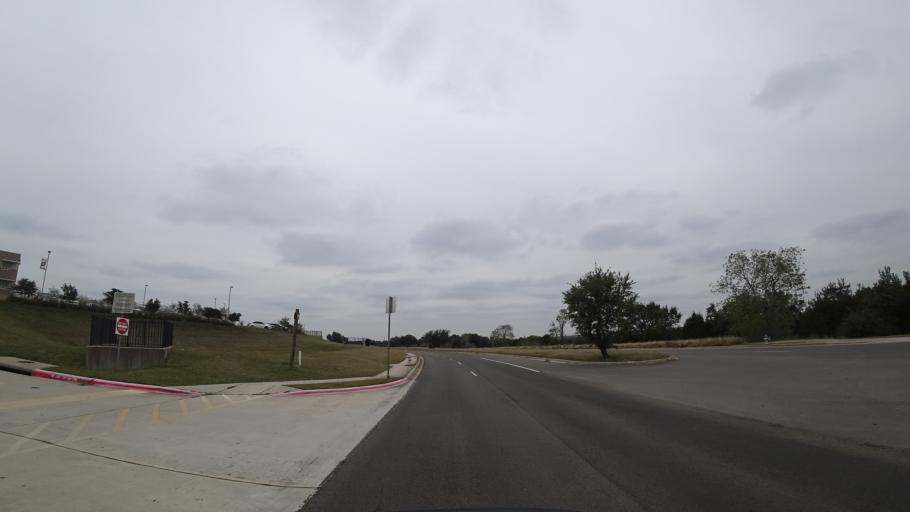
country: US
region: Texas
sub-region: Travis County
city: Shady Hollow
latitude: 30.2141
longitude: -97.8931
